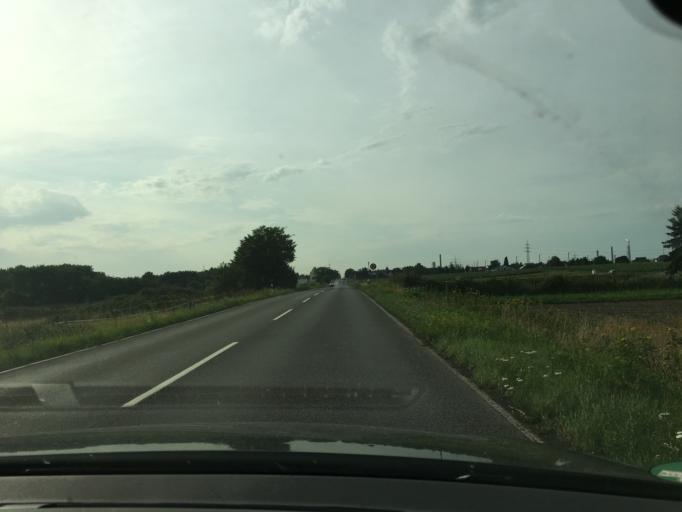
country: DE
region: North Rhine-Westphalia
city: Niederkassel
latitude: 50.7990
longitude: 7.0179
